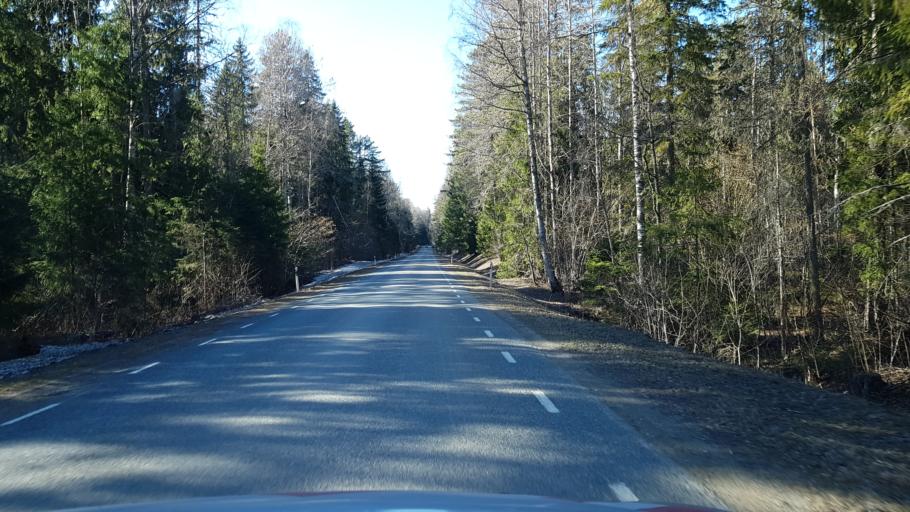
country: EE
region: Laeaene-Virumaa
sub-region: Vinni vald
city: Vinni
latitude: 59.2660
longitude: 26.6722
